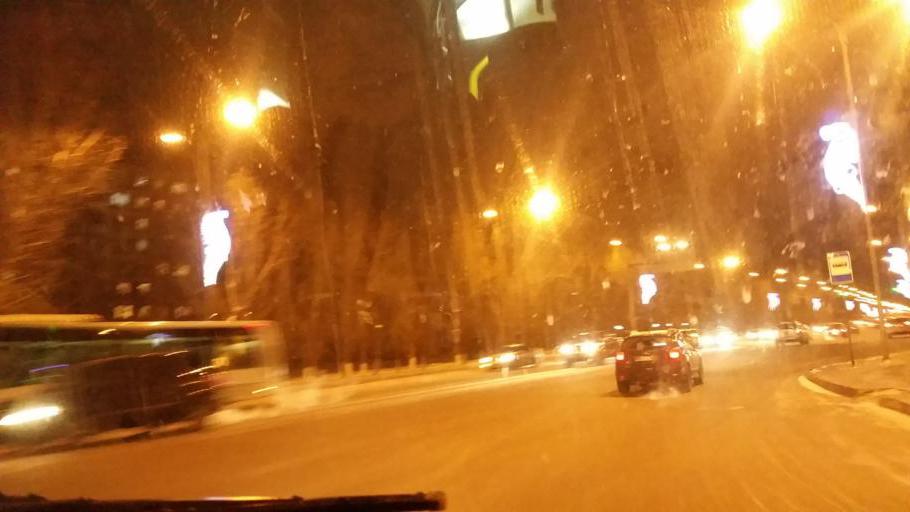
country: KZ
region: Astana Qalasy
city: Astana
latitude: 51.1572
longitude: 71.4788
